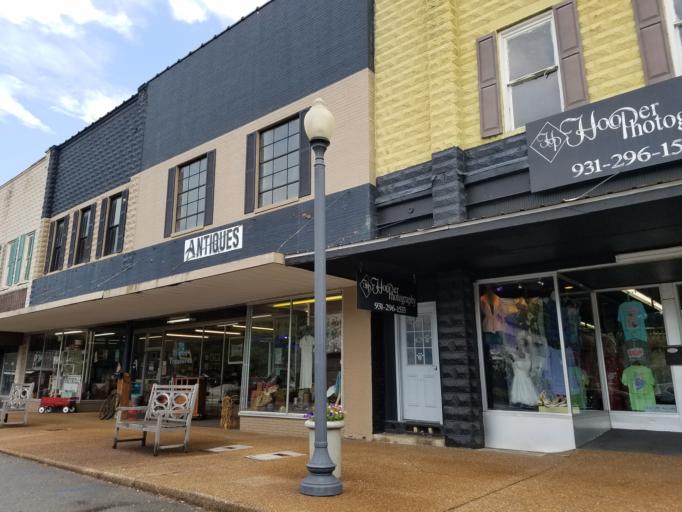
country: US
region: Tennessee
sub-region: Humphreys County
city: Waverly
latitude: 36.0831
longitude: -87.7940
